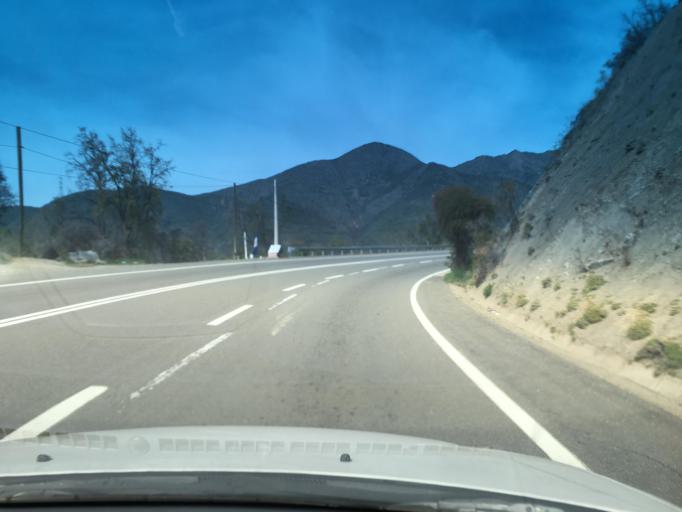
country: CL
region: Valparaiso
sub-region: Provincia de San Felipe
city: Llaillay
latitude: -33.0653
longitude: -70.9897
